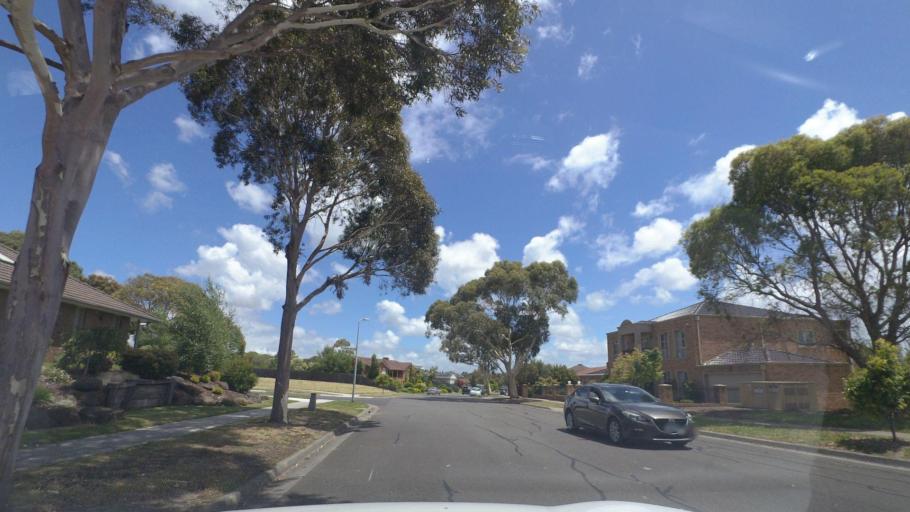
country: AU
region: Victoria
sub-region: Knox
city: Ferntree Gully
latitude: -37.9071
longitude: 145.2764
